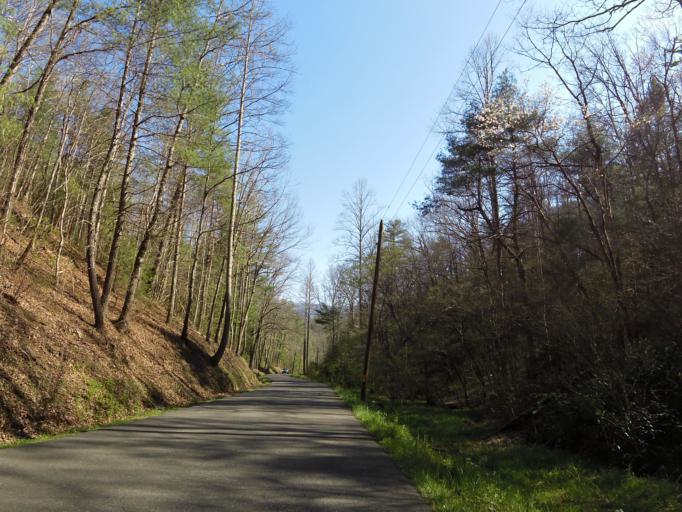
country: US
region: Tennessee
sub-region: Sevier County
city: Pigeon Forge
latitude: 35.6915
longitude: -83.6458
